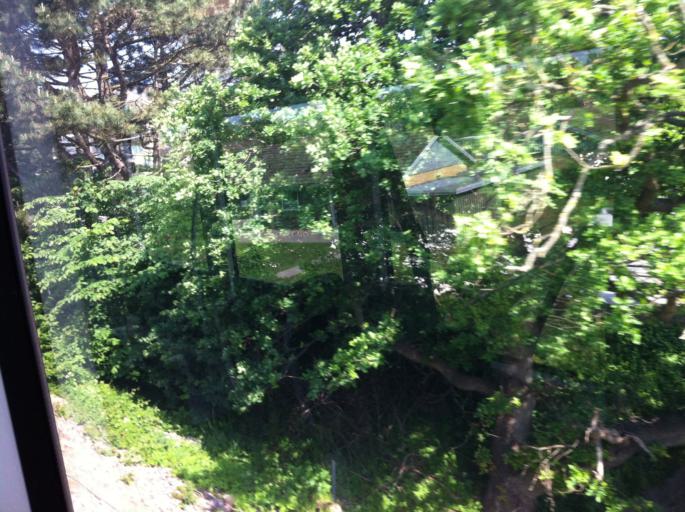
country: DK
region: Capital Region
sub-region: Gribskov Kommune
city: Gilleleje
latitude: 56.1237
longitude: 12.3067
